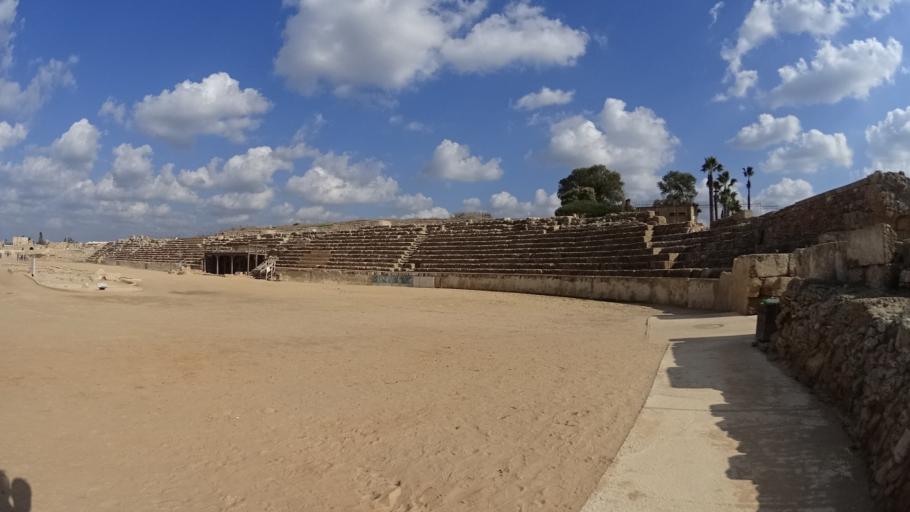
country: IL
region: Haifa
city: Qesarya
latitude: 32.4973
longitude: 34.8903
